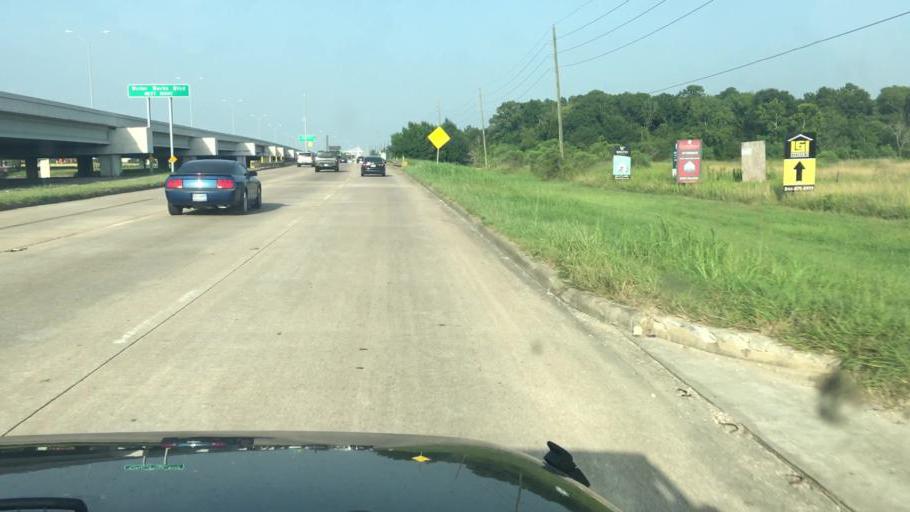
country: US
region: Texas
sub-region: Harris County
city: Humble
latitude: 29.9338
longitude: -95.2357
